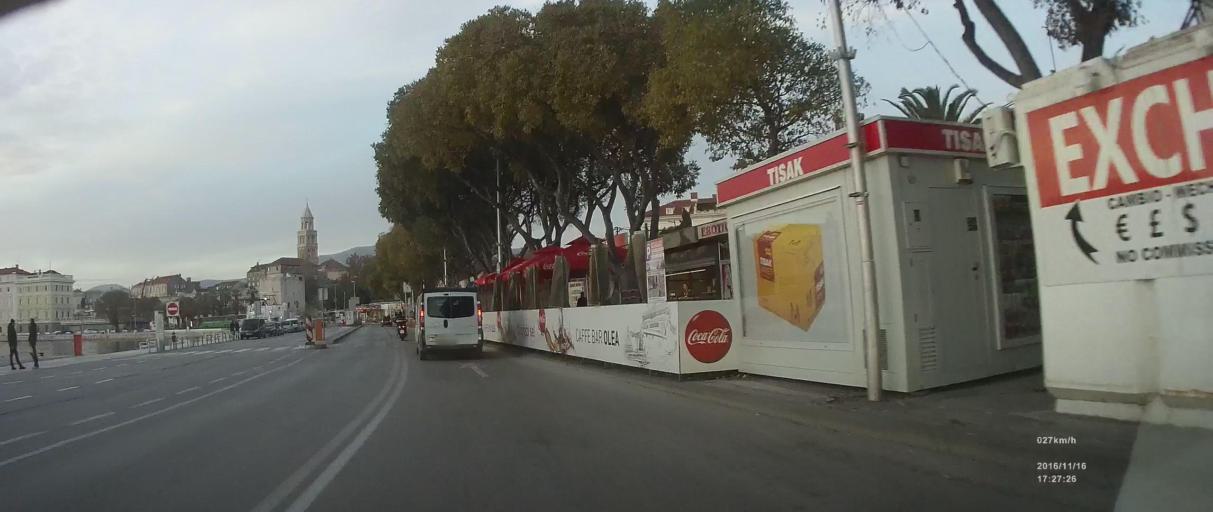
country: HR
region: Splitsko-Dalmatinska
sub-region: Grad Split
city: Split
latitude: 43.5050
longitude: 16.4423
